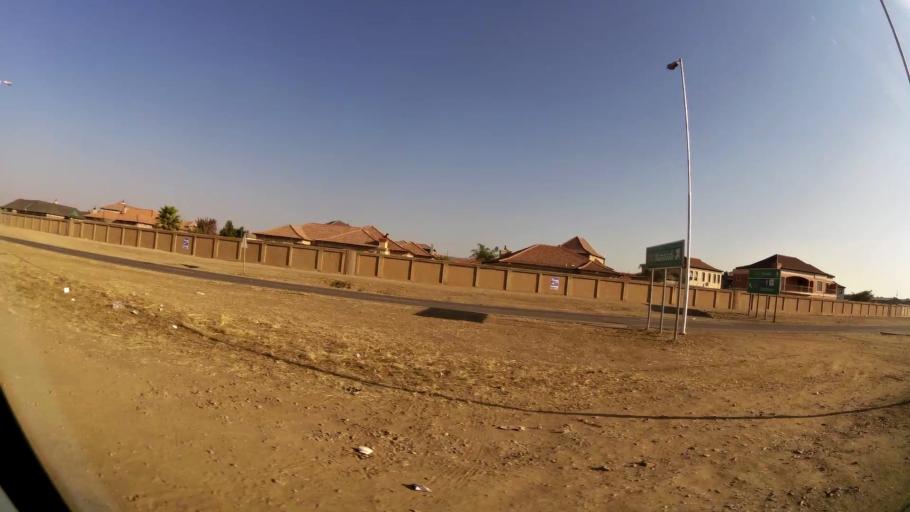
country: ZA
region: Gauteng
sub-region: City of Tshwane Metropolitan Municipality
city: Cullinan
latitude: -25.7518
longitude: 28.3702
